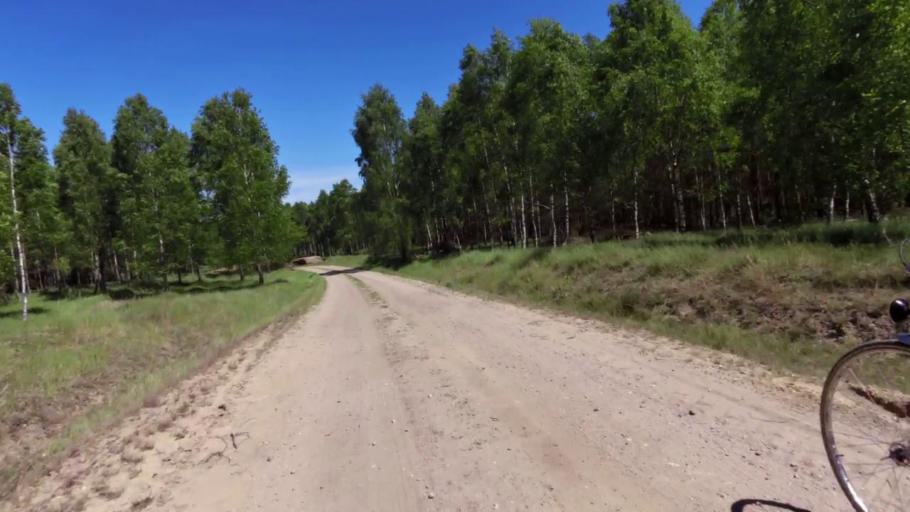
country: PL
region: West Pomeranian Voivodeship
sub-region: Powiat szczecinecki
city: Borne Sulinowo
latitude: 53.5762
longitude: 16.6399
